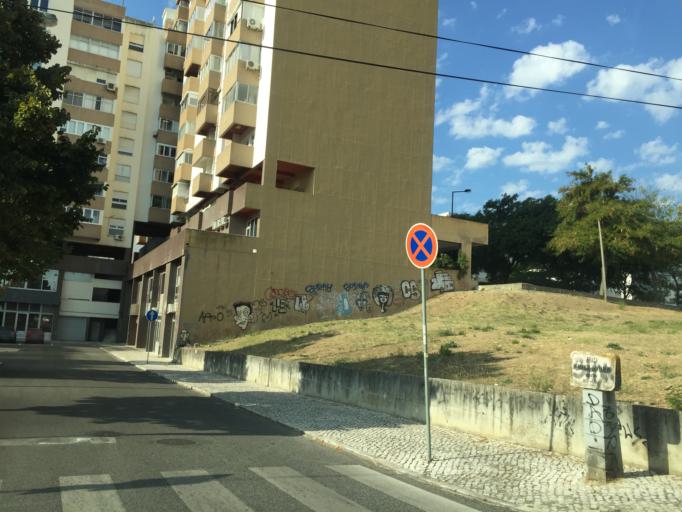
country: PT
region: Lisbon
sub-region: Lisbon
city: Lisbon
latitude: 38.7444
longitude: -9.1281
